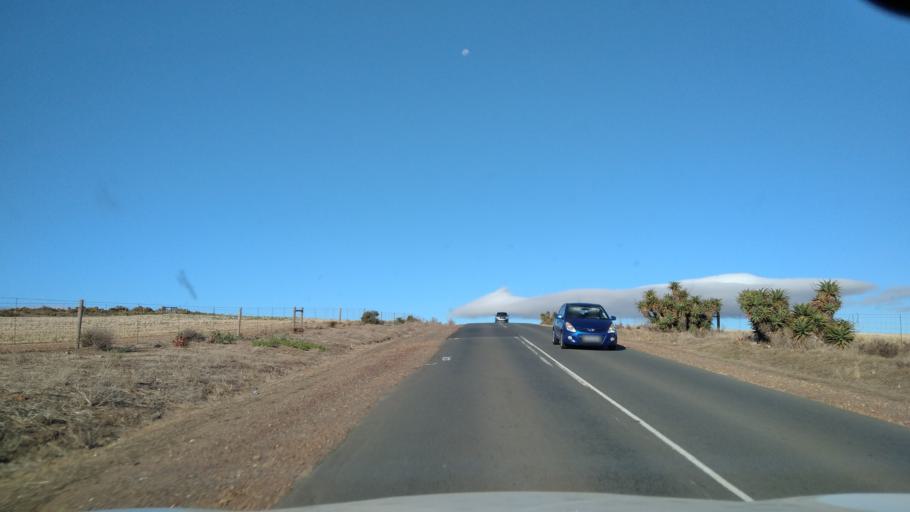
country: ZA
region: Western Cape
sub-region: Overberg District Municipality
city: Caledon
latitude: -34.1699
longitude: 19.2882
